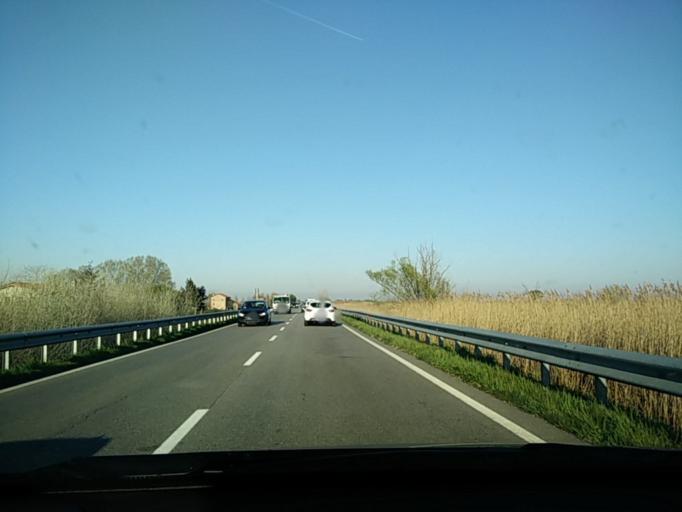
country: IT
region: Veneto
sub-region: Provincia di Venezia
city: Musile di Piave
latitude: 45.5726
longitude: 12.5174
